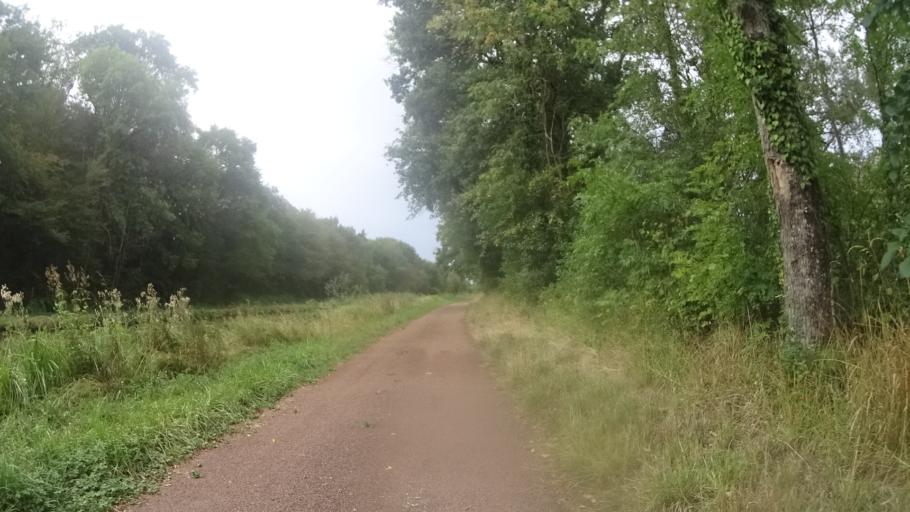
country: FR
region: Bourgogne
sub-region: Departement de la Nievre
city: Imphy
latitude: 46.9157
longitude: 3.2424
